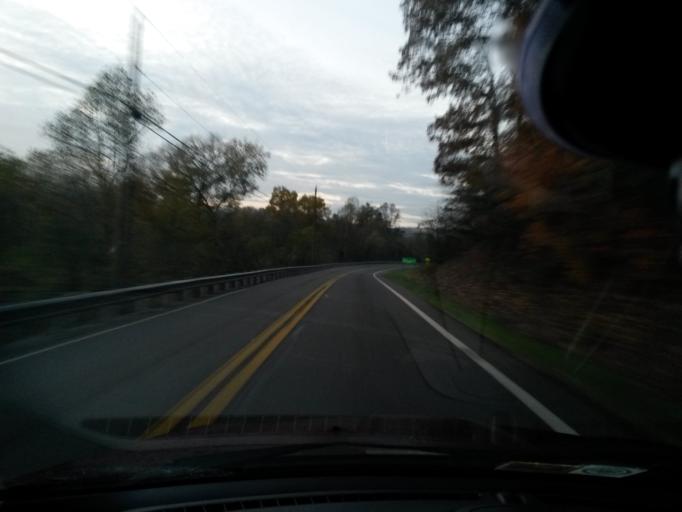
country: US
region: Virginia
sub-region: Alleghany County
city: Clifton Forge
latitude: 37.7825
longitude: -79.7794
